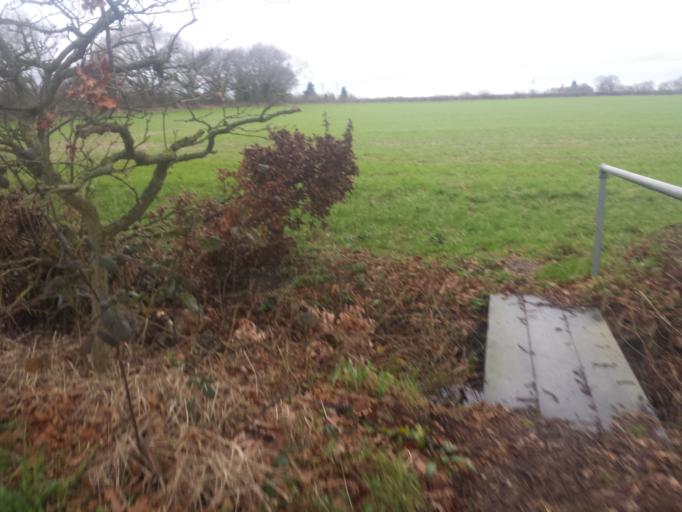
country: GB
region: England
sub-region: Essex
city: Great Bentley
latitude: 51.8881
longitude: 1.0429
